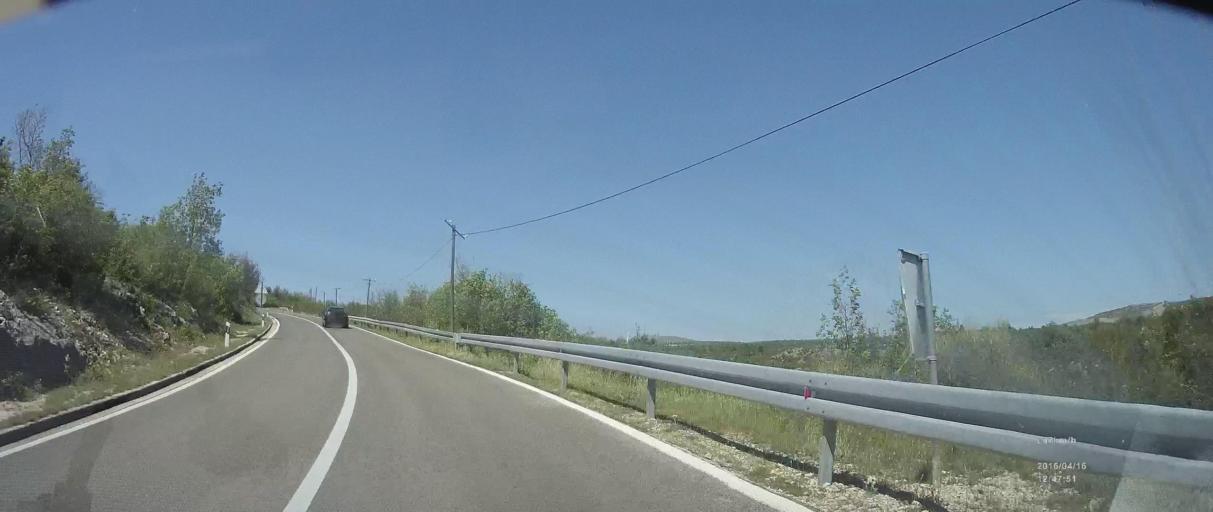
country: HR
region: Sibensko-Kniniska
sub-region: Grad Sibenik
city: Brodarica
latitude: 43.6680
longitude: 16.0445
